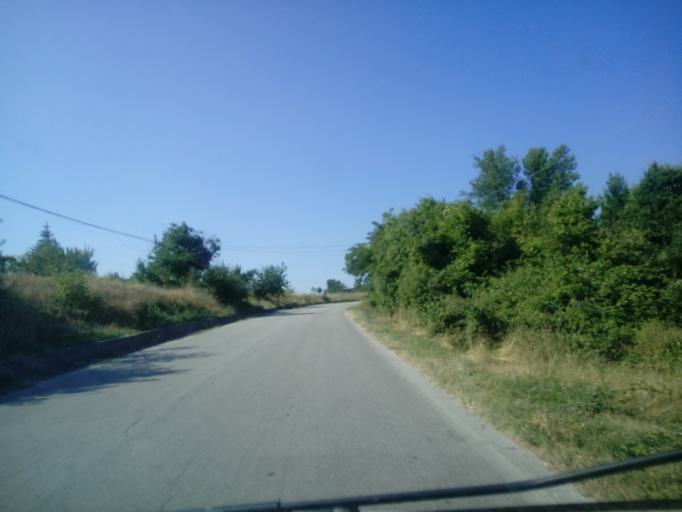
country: IT
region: Molise
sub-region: Provincia di Campobasso
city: Jelsi
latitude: 41.5122
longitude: 14.7891
